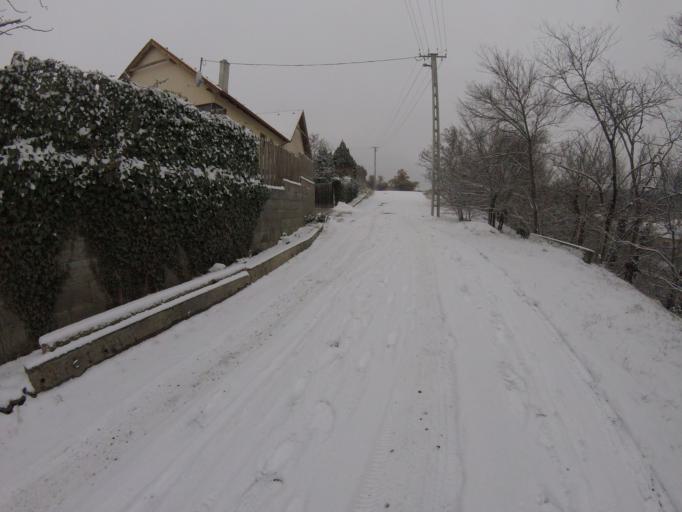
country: HU
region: Fejer
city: Pakozd
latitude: 47.2191
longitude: 18.5405
